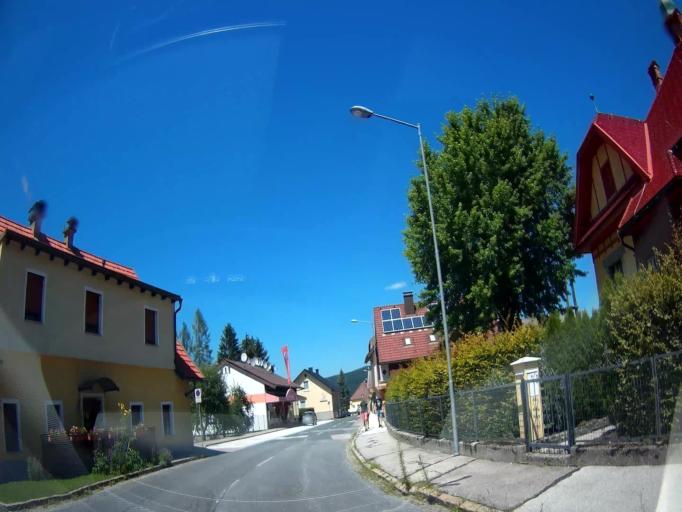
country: AT
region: Carinthia
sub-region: Politischer Bezirk Klagenfurt Land
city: Ferlach
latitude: 46.5237
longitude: 14.3007
